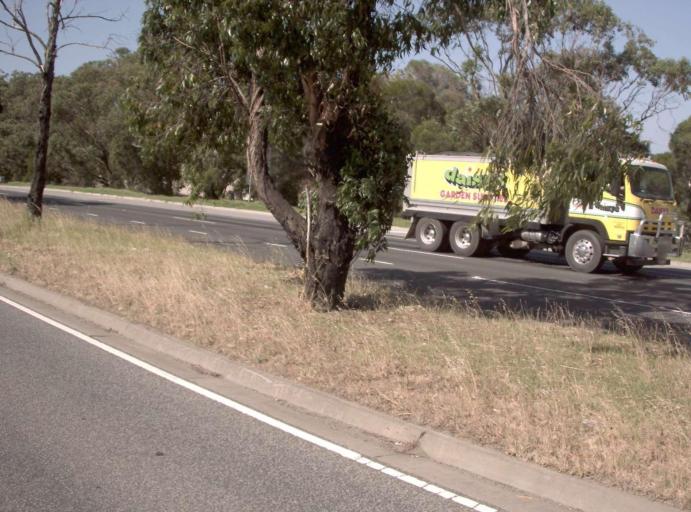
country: AU
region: Victoria
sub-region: Casey
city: Hampton Park
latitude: -38.0389
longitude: 145.2104
